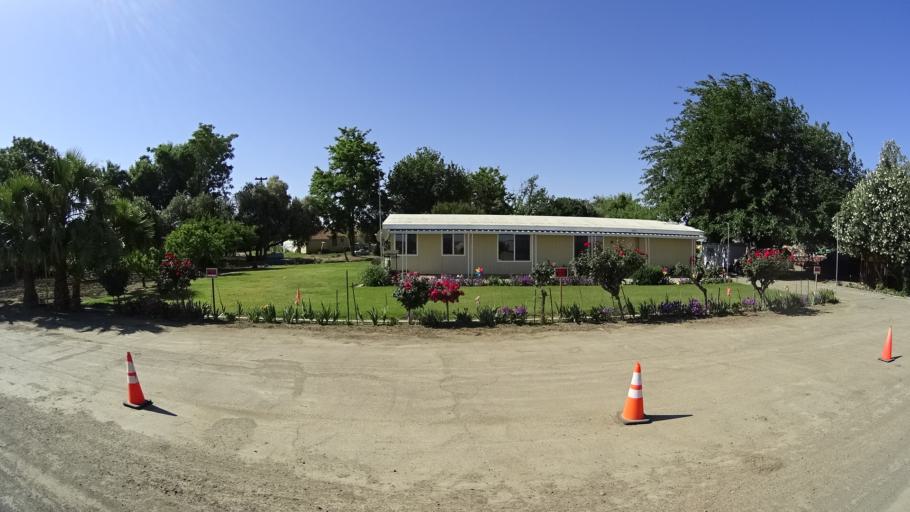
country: US
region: California
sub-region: Kings County
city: Lemoore Station
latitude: 36.1814
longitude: -119.9574
